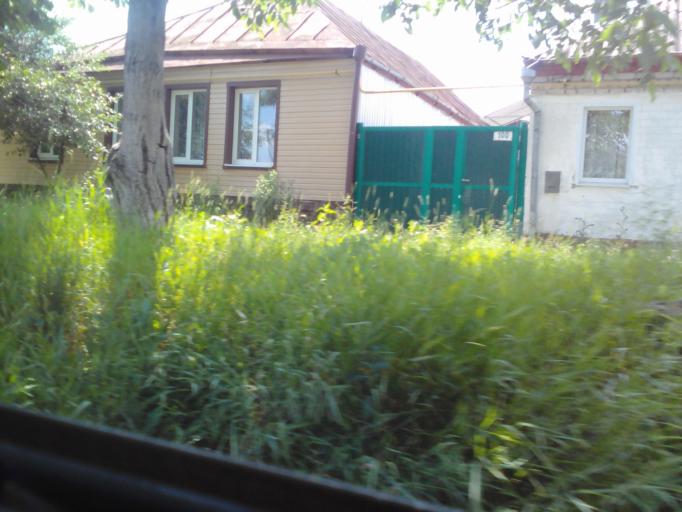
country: RU
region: Kursk
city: Kursk
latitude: 51.7386
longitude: 36.1739
